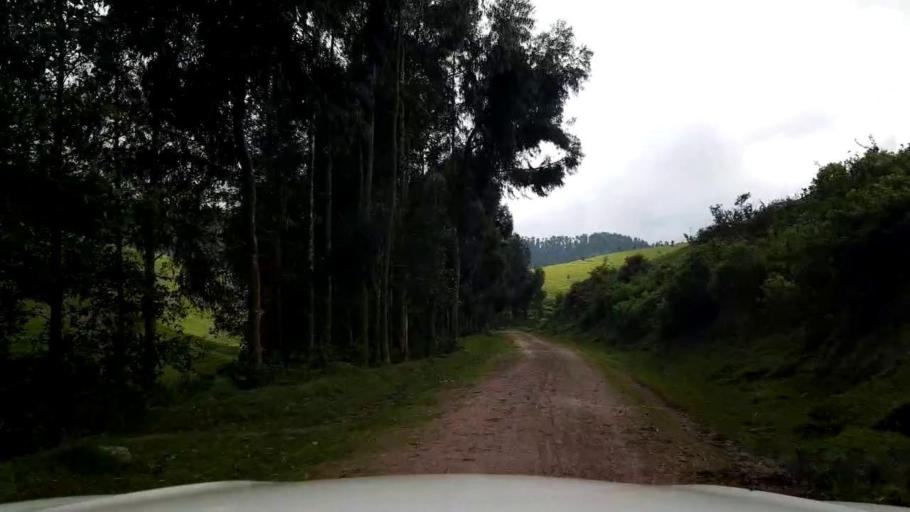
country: RW
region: Western Province
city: Gisenyi
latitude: -1.6868
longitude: 29.4212
